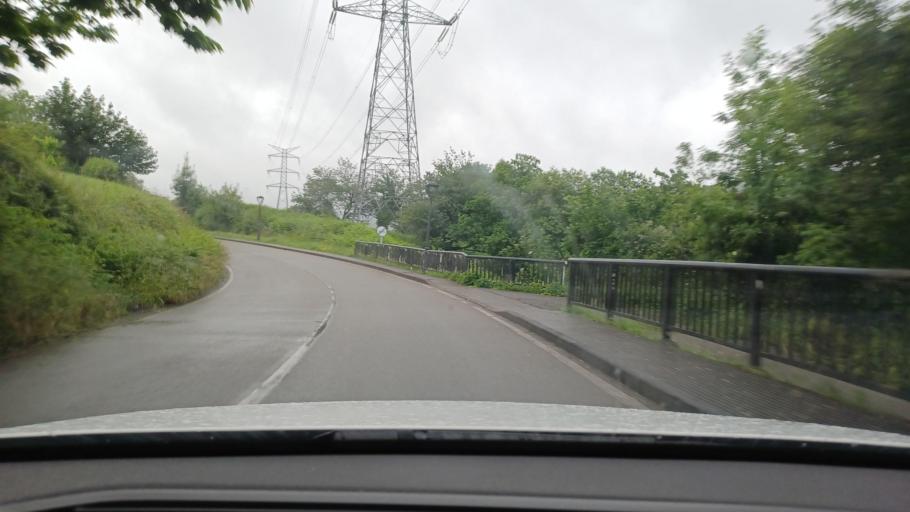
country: ES
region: Asturias
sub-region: Province of Asturias
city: Castandiello
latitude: 43.3116
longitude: -5.8768
